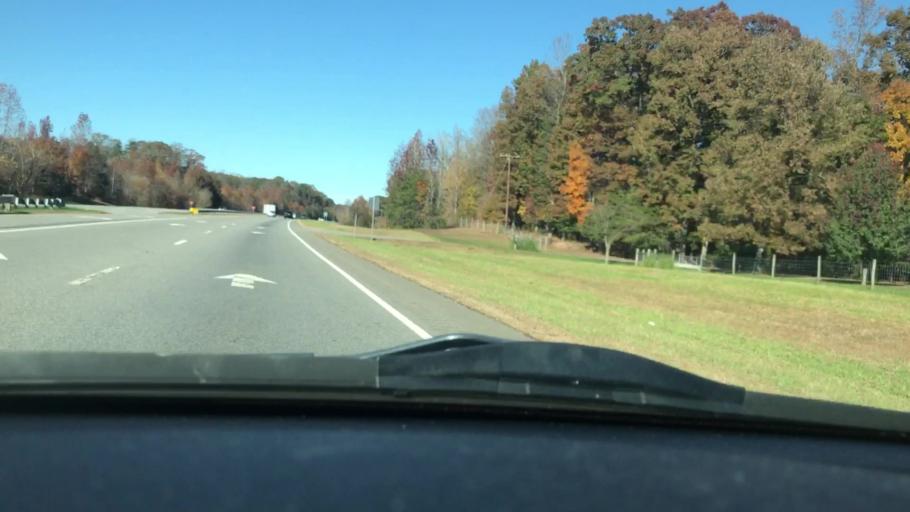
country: US
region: North Carolina
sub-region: Rockingham County
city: Madison
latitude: 36.3907
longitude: -79.9410
